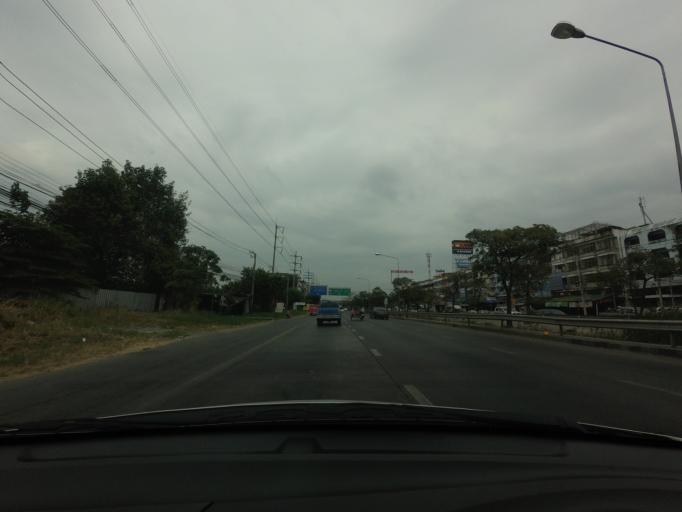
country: TH
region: Samut Prakan
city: Samut Prakan
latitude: 13.6103
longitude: 100.6175
